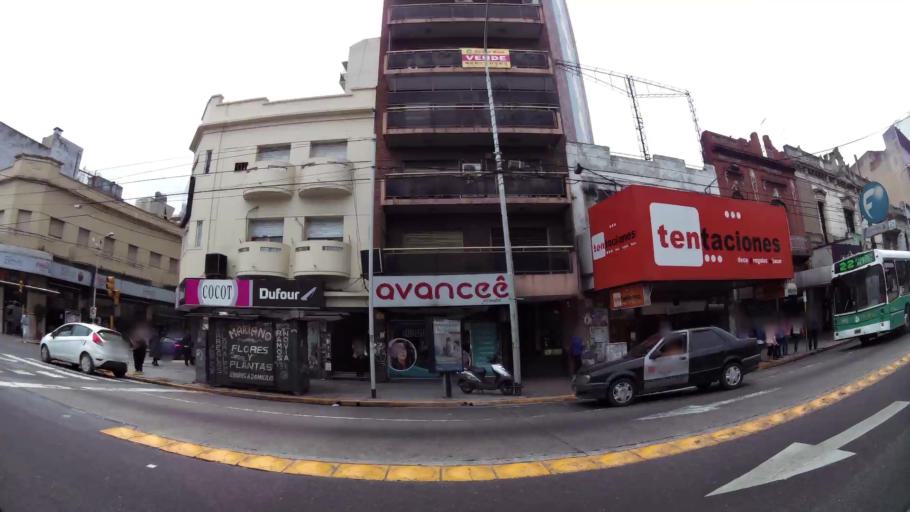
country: AR
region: Buenos Aires
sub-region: Partido de Avellaneda
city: Avellaneda
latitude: -34.6629
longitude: -58.3642
